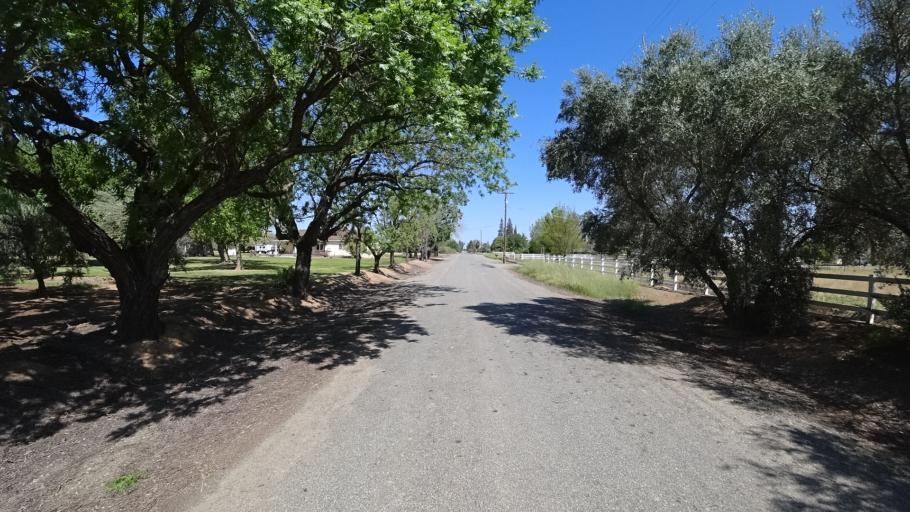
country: US
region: California
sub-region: Glenn County
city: Orland
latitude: 39.7906
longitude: -122.1504
